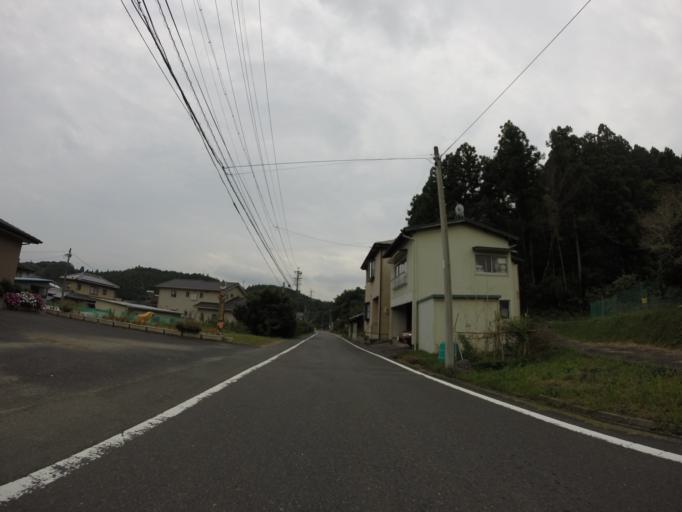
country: JP
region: Shizuoka
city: Kakegawa
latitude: 34.8192
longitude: 138.0180
